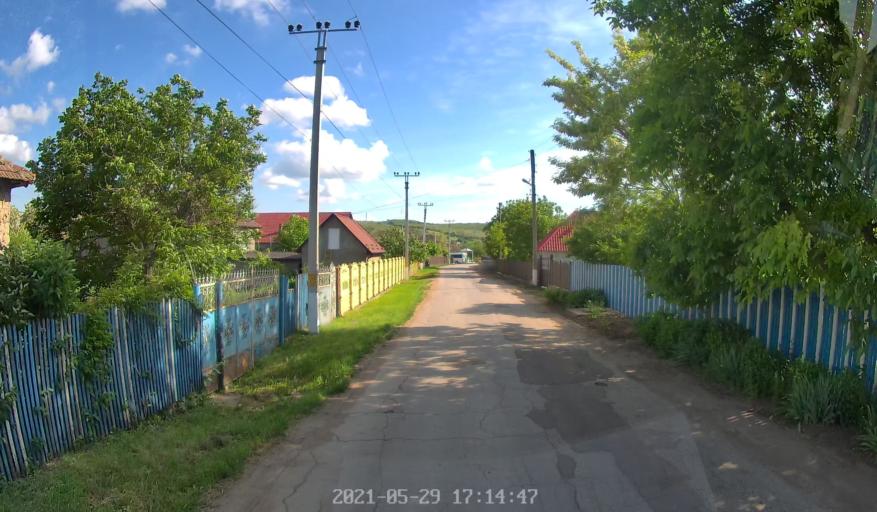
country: MD
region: Laloveni
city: Ialoveni
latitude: 46.8346
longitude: 28.8480
